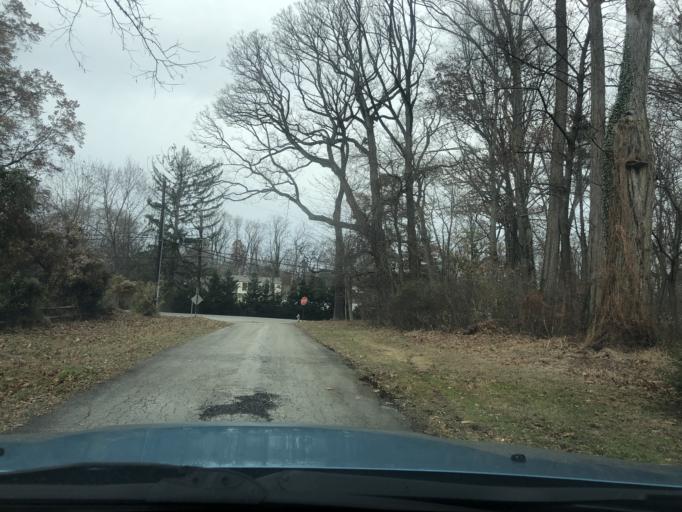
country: US
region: Pennsylvania
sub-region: Delaware County
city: Radnor
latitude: 40.0336
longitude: -75.3536
